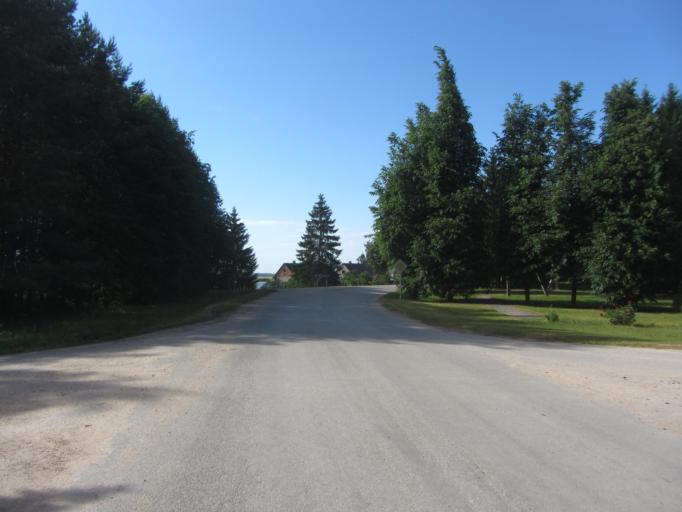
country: LT
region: Panevezys
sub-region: Birzai
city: Birzai
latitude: 56.2996
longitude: 24.6227
